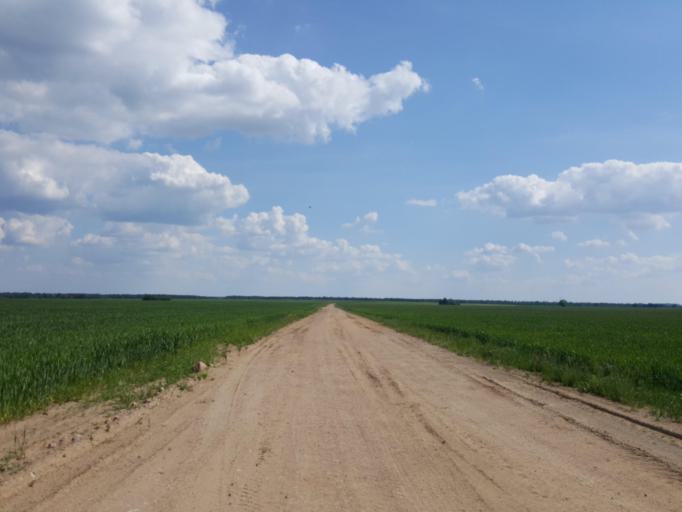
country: BY
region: Brest
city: Kamyanyuki
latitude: 52.4894
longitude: 23.5990
